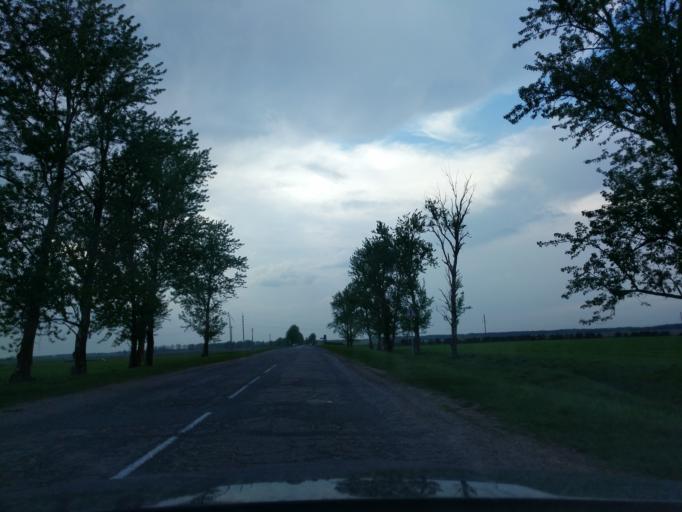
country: BY
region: Minsk
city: Novy Svyerzhan'
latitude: 53.4772
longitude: 26.6298
